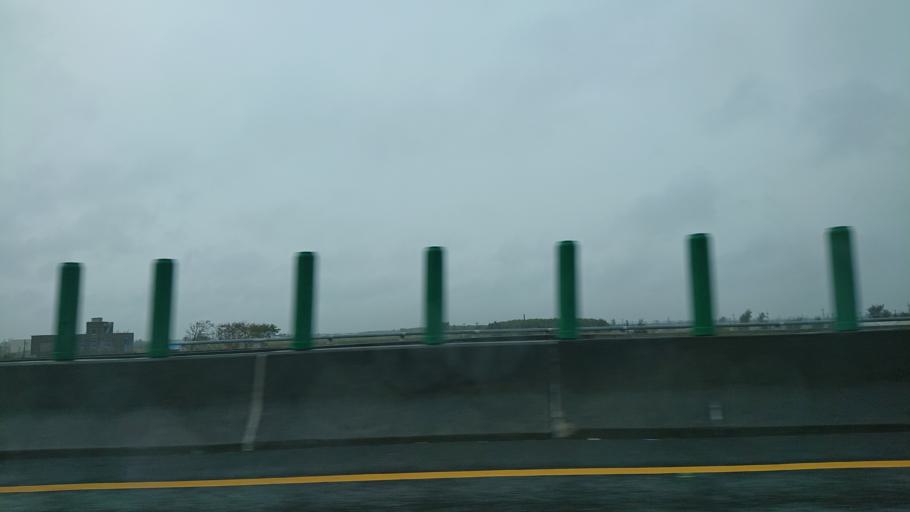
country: TW
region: Taiwan
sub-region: Chiayi
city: Taibao
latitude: 23.7212
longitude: 120.2161
